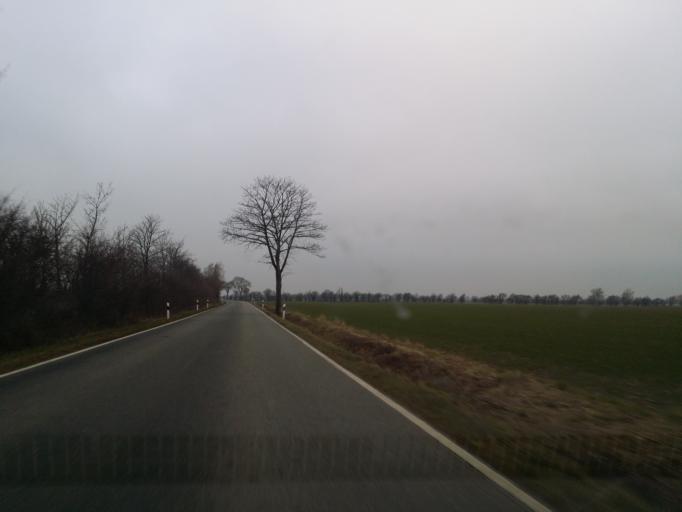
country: DE
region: Schleswig-Holstein
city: Fehmarn
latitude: 54.4654
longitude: 11.1141
